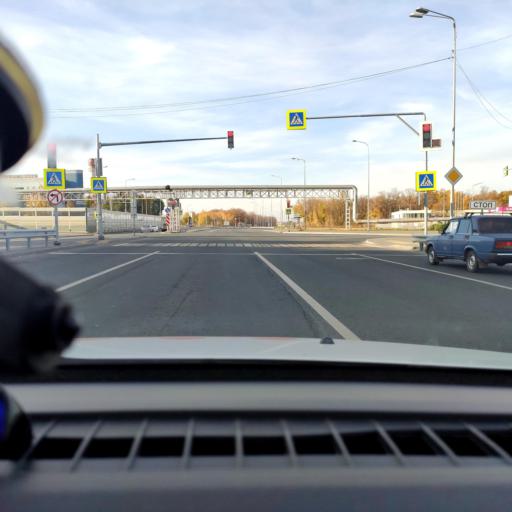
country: RU
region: Samara
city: Bereza
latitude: 53.5121
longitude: 50.1449
